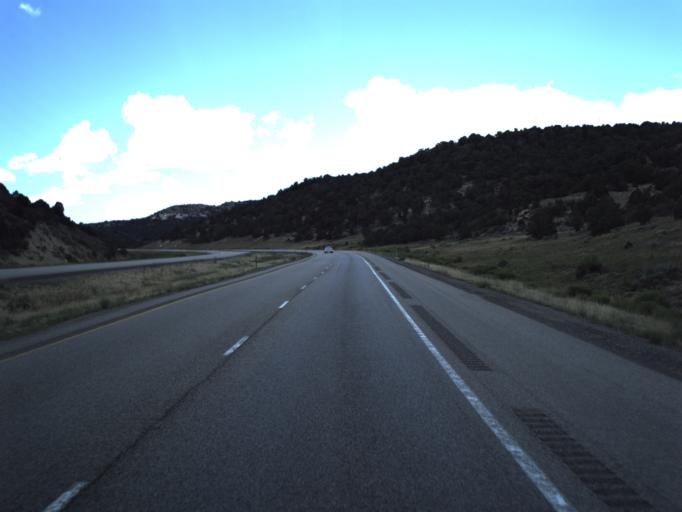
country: US
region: Utah
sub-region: Wayne County
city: Loa
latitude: 38.7701
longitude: -111.4723
